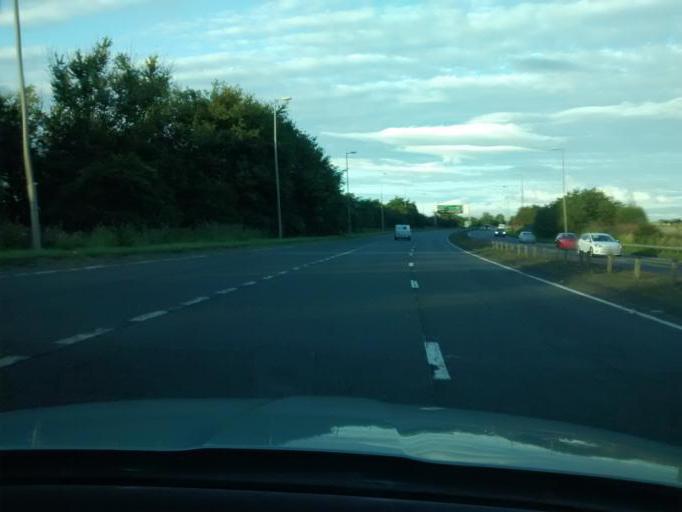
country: GB
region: Scotland
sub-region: Renfrewshire
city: Elderslie
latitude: 55.8498
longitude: -4.4775
